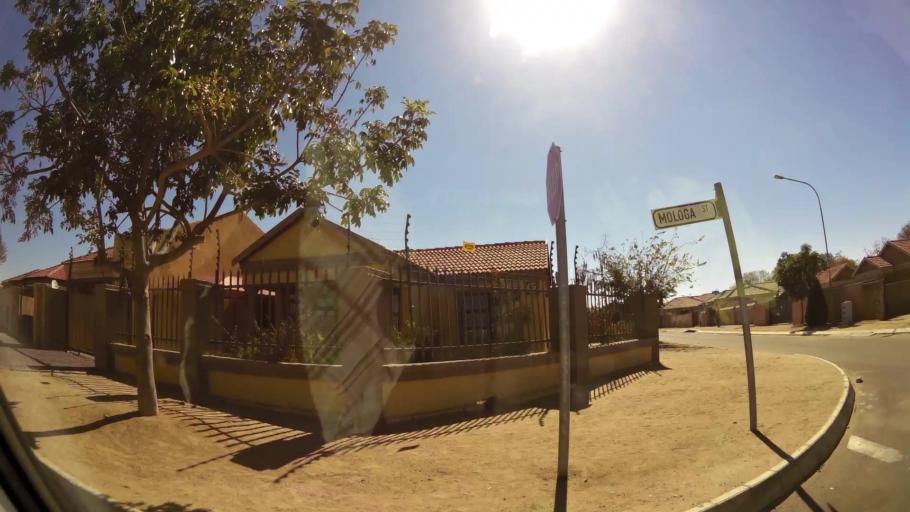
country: ZA
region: Limpopo
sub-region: Capricorn District Municipality
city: Polokwane
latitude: -23.8599
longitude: 29.4263
